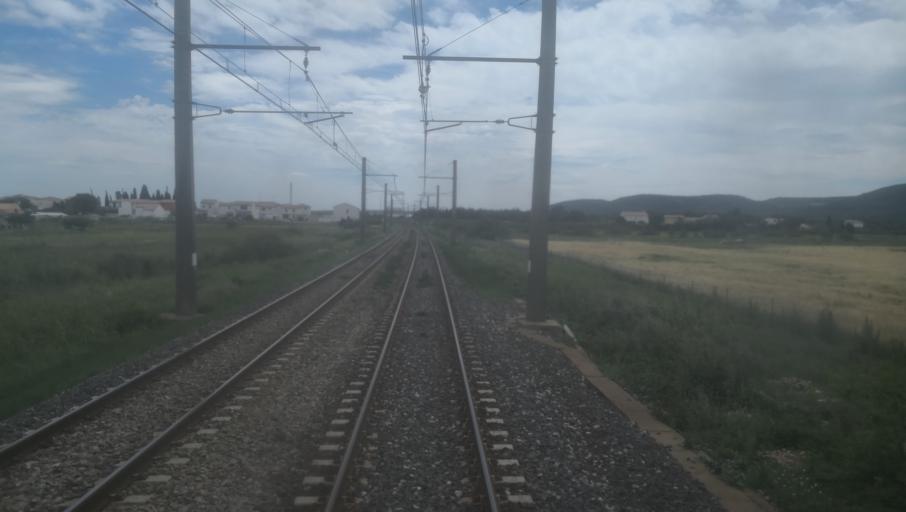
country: FR
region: Languedoc-Roussillon
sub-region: Departement de l'Herault
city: Vic-la-Gardiole
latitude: 43.4944
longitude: 3.7925
